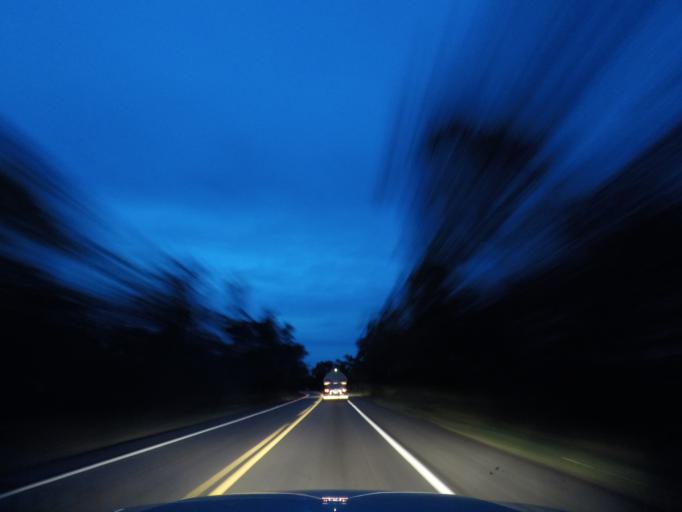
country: BR
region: Bahia
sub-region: Andarai
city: Vera Cruz
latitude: -12.4850
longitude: -41.3452
